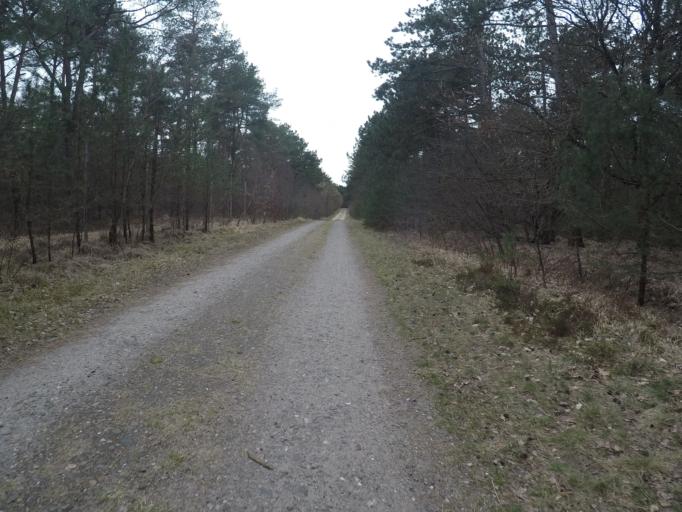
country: DE
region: Lower Saxony
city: Nordholz
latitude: 53.8062
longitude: 8.6254
